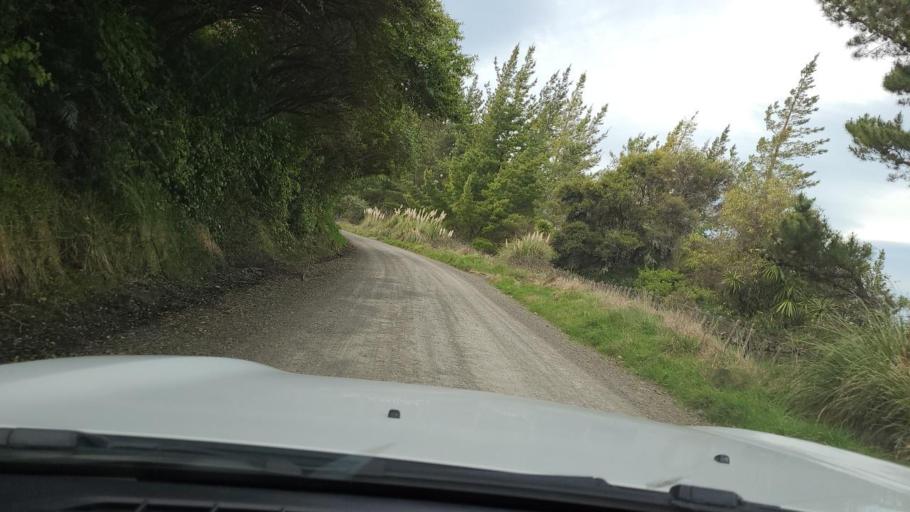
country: NZ
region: Hawke's Bay
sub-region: Napier City
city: Napier
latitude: -39.2922
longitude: 176.8374
